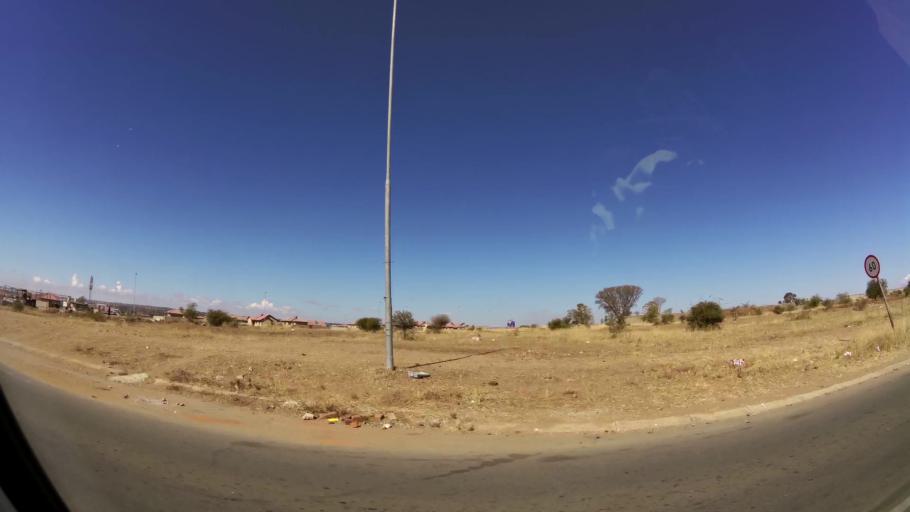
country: ZA
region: Limpopo
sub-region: Capricorn District Municipality
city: Polokwane
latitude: -23.8702
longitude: 29.4245
